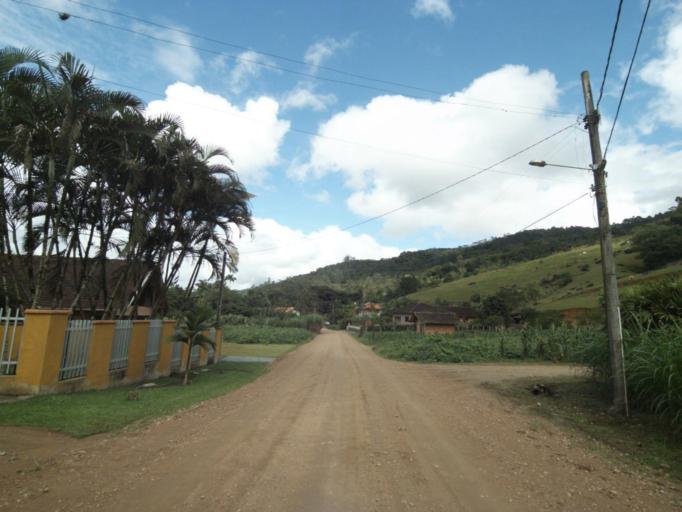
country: BR
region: Santa Catarina
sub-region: Pomerode
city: Pomerode
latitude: -26.6763
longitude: -49.1872
